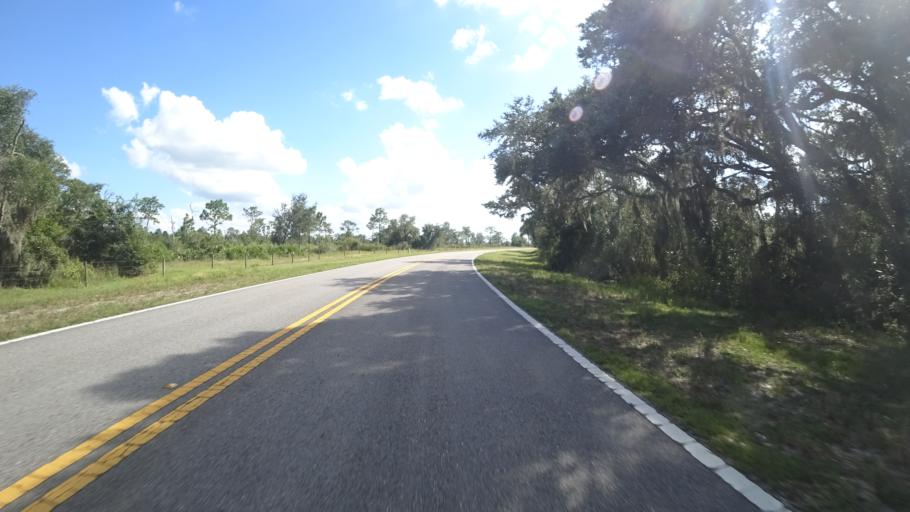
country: US
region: Florida
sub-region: Sarasota County
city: The Meadows
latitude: 27.4832
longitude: -82.3514
